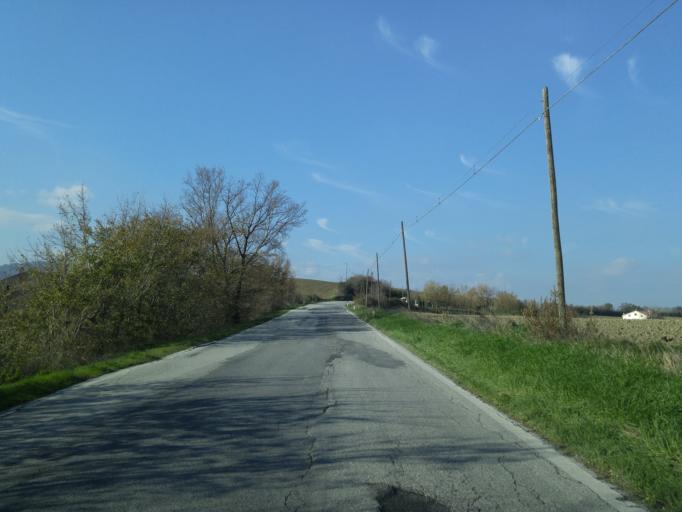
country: IT
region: The Marches
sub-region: Provincia di Pesaro e Urbino
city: Lucrezia
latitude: 43.7964
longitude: 12.9209
